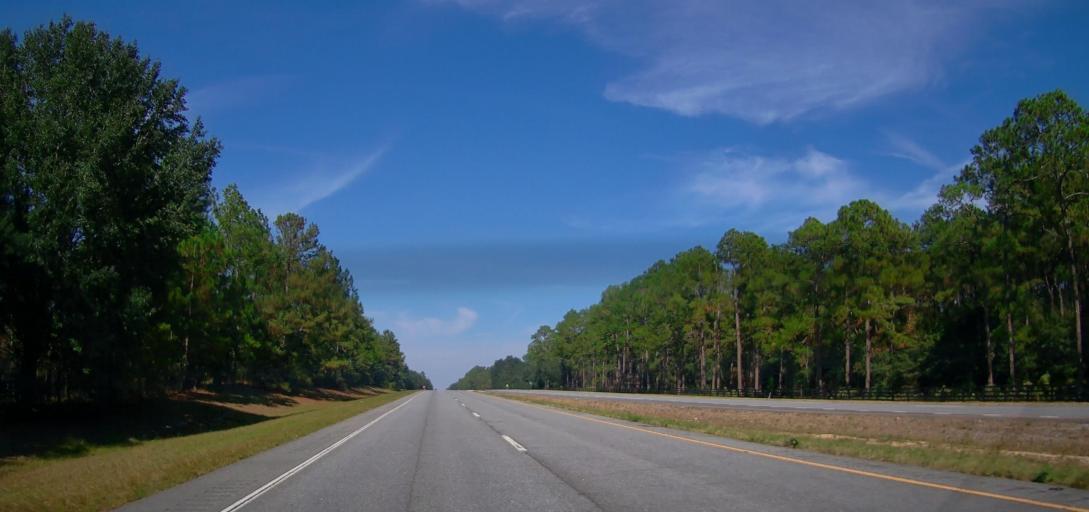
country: US
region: Georgia
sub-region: Lee County
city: Leesburg
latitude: 31.6812
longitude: -83.9946
